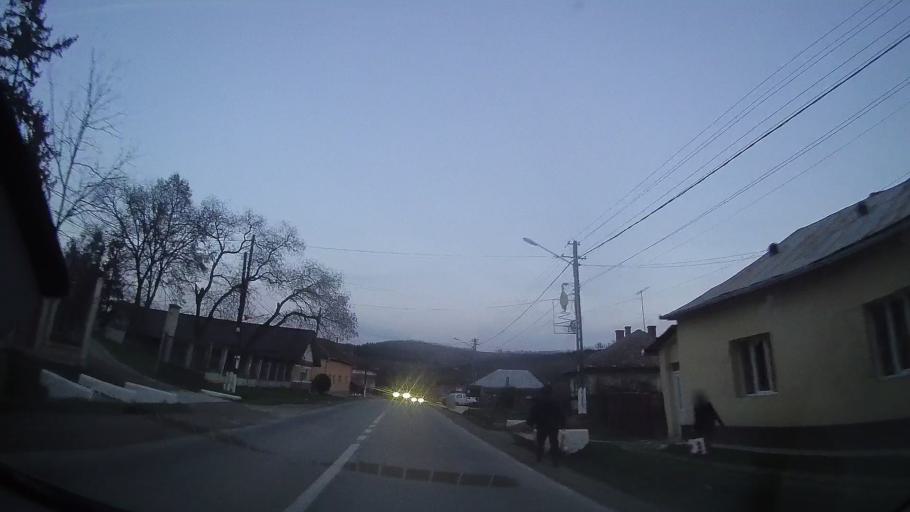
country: RO
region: Cluj
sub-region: Comuna Mociu
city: Mociu
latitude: 46.7993
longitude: 24.0367
